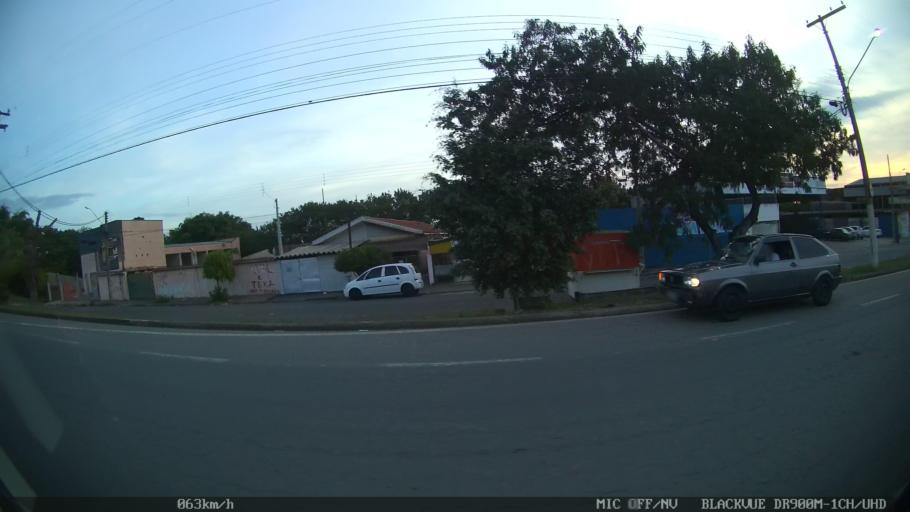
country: BR
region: Sao Paulo
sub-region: Limeira
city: Limeira
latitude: -22.5513
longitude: -47.3832
